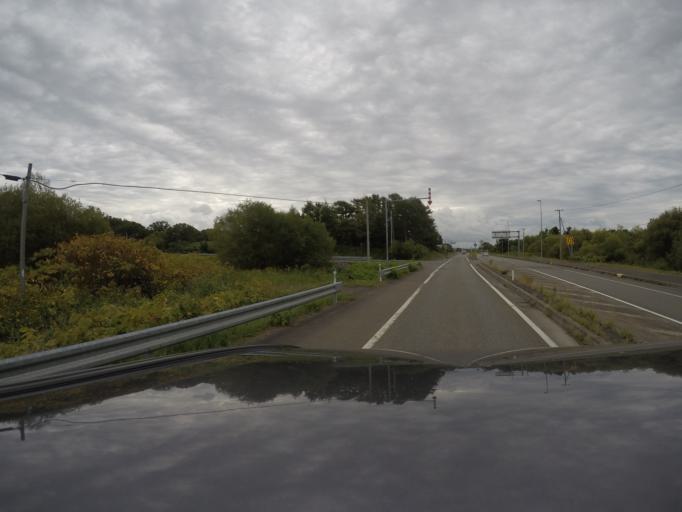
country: JP
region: Hokkaido
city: Makubetsu
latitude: 45.1474
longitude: 141.7517
